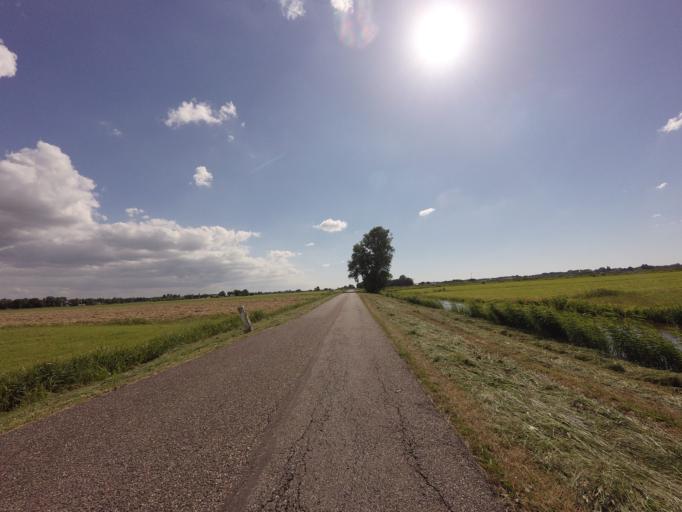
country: NL
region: Utrecht
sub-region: Gemeente De Ronde Venen
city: Mijdrecht
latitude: 52.2291
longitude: 4.8656
